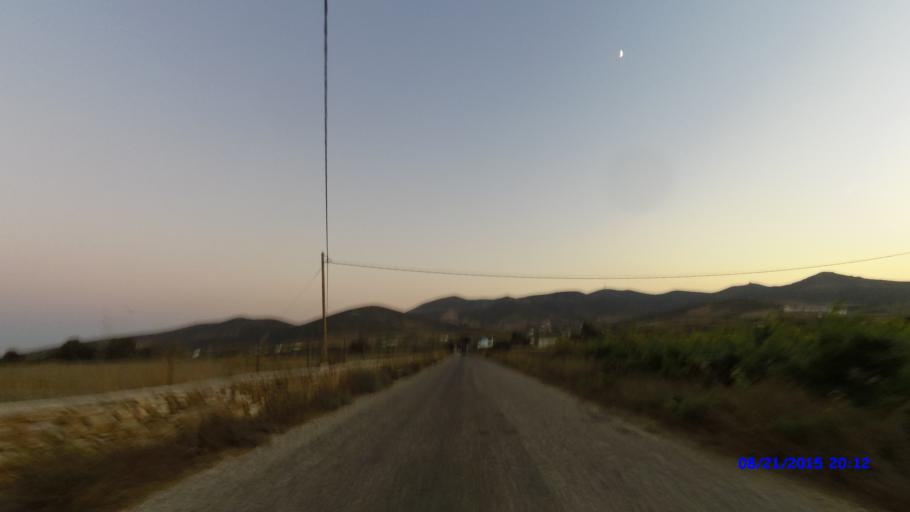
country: GR
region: South Aegean
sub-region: Nomos Kykladon
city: Antiparos
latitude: 37.0165
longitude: 25.0603
